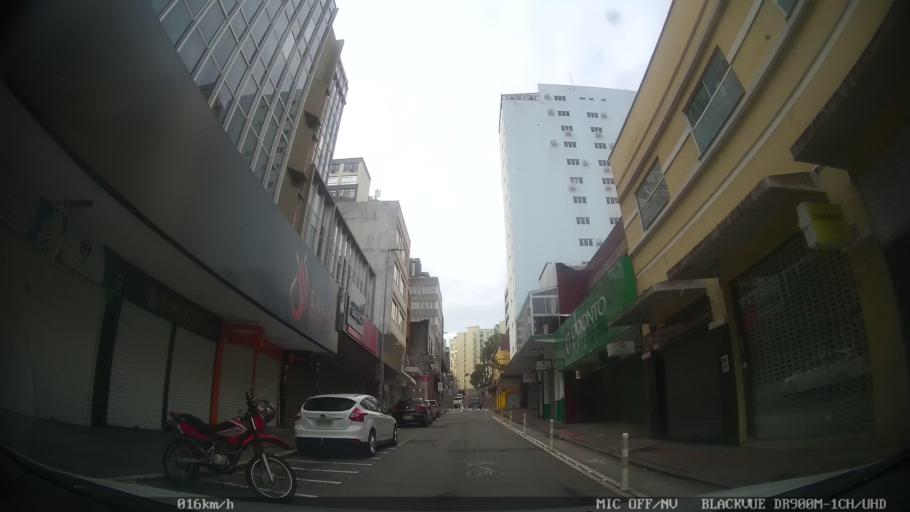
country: BR
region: Santa Catarina
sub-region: Florianopolis
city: Florianopolis
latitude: -27.5960
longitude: -48.5535
